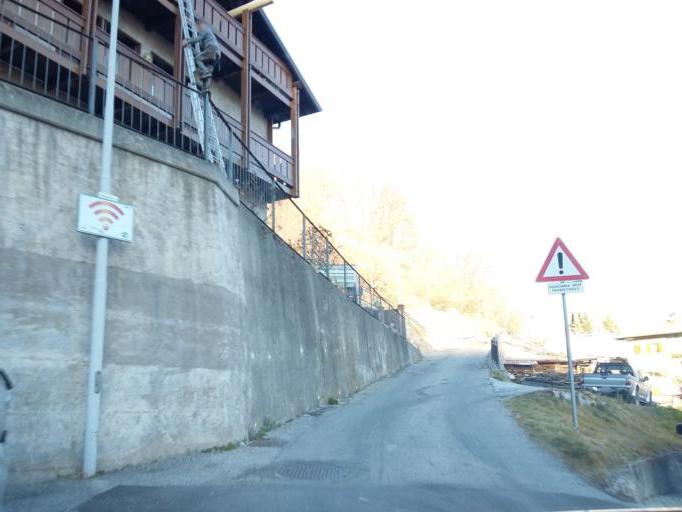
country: IT
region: Trentino-Alto Adige
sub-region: Provincia di Trento
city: Brione
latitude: 45.8949
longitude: 10.5882
